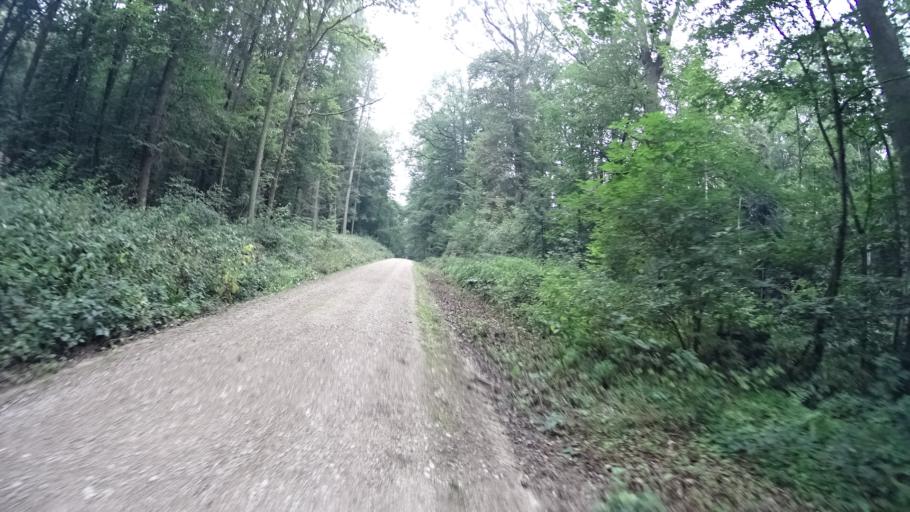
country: DE
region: Bavaria
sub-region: Upper Bavaria
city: Stammham
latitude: 48.8369
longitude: 11.4872
